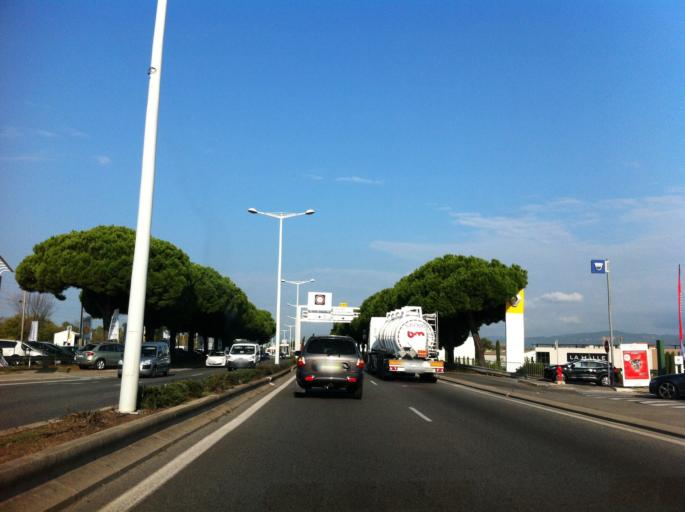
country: FR
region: Provence-Alpes-Cote d'Azur
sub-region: Departement du Var
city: Frejus
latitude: 43.4353
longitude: 6.7248
